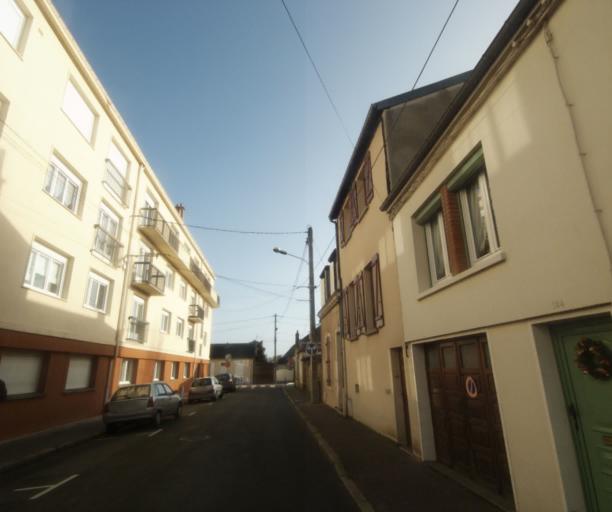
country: FR
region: Pays de la Loire
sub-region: Departement de la Sarthe
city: Le Mans
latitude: 47.9928
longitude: 0.2101
